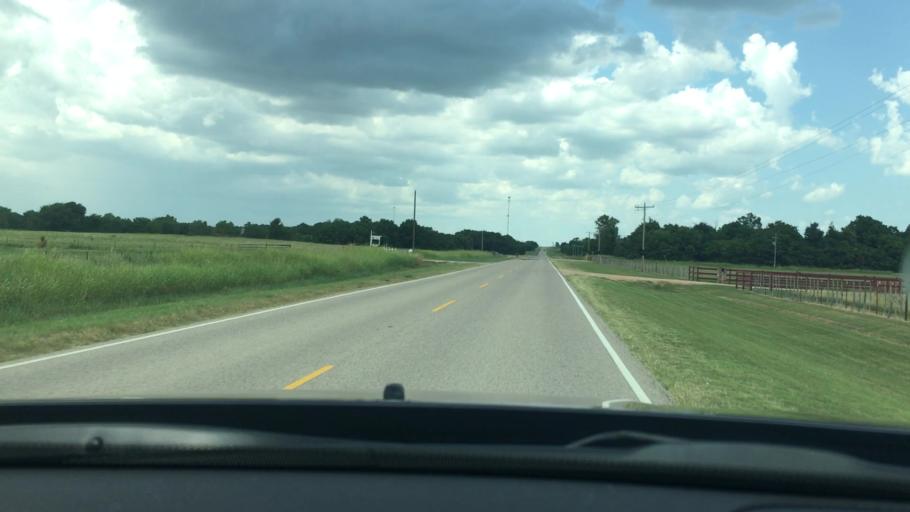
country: US
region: Oklahoma
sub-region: Johnston County
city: Tishomingo
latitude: 34.4169
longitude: -96.6359
